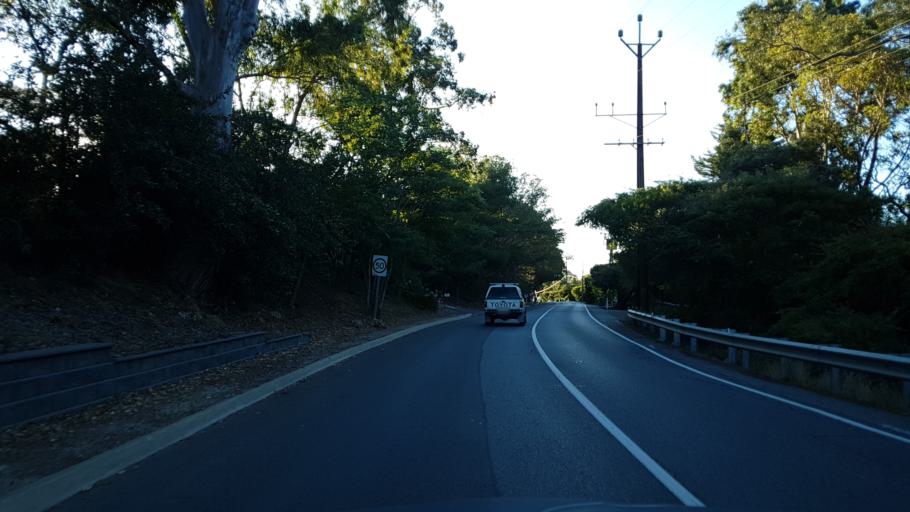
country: AU
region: South Australia
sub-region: Tea Tree Gully
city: Golden Grove
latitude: -34.8254
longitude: 138.7769
